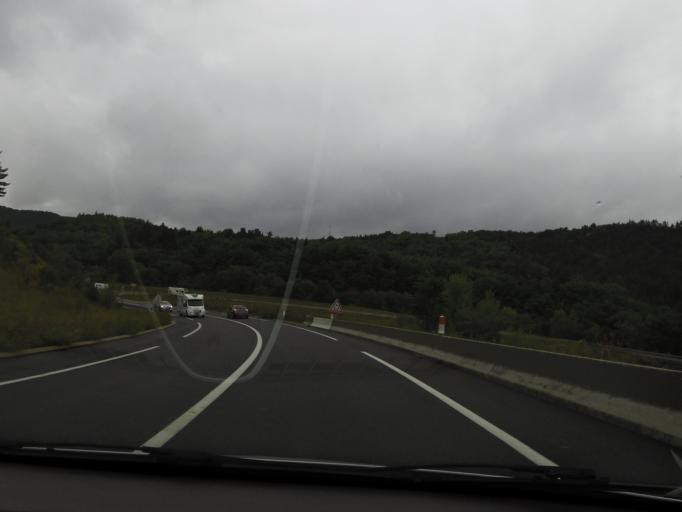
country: FR
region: Languedoc-Roussillon
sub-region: Departement de la Lozere
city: Chirac
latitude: 44.4975
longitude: 3.2650
